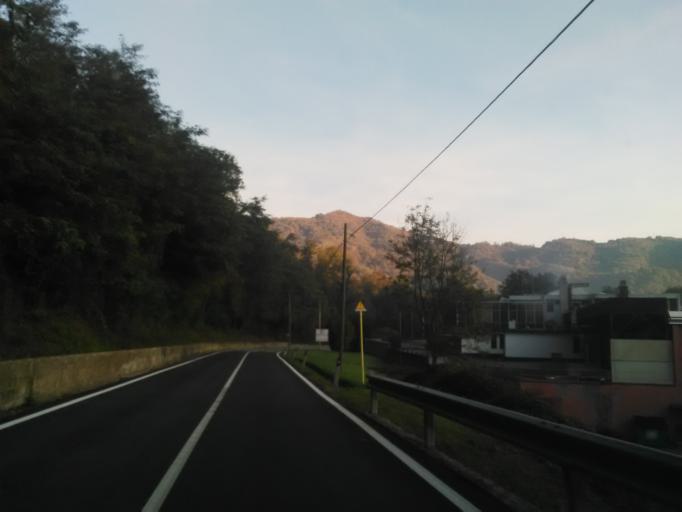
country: IT
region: Piedmont
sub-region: Provincia di Vercelli
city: Guardabosone
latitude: 45.6929
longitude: 8.2639
